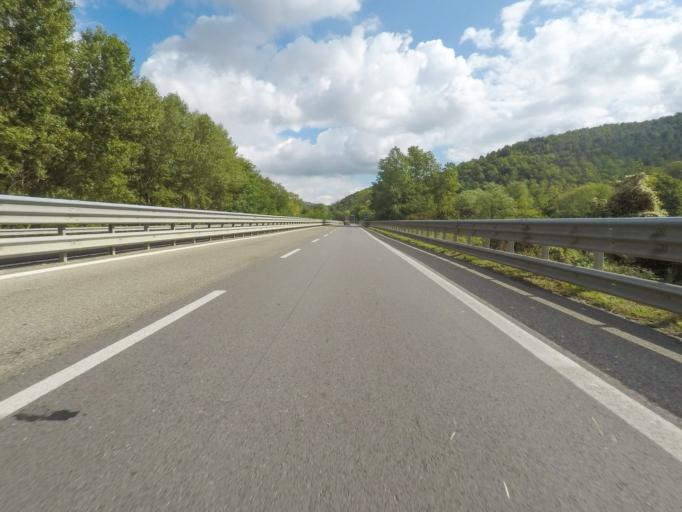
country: IT
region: Tuscany
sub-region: Provincia di Siena
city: Serre di Rapolano
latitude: 43.2528
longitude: 11.6809
